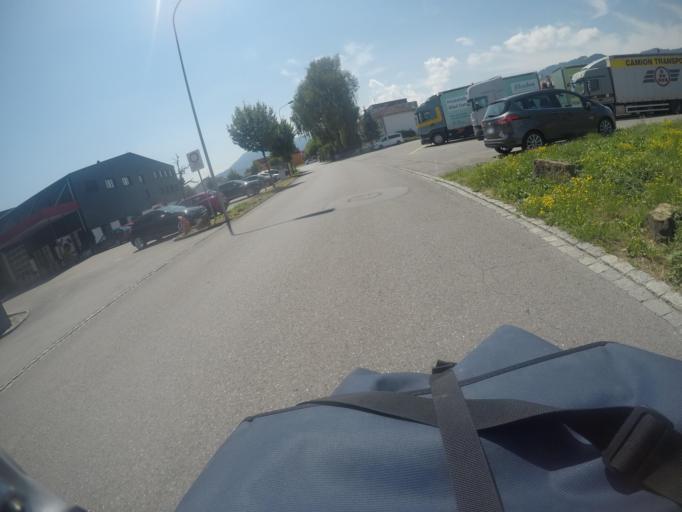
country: CH
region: Saint Gallen
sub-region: Wahlkreis Rheintal
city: Altstatten
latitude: 47.3760
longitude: 9.5596
